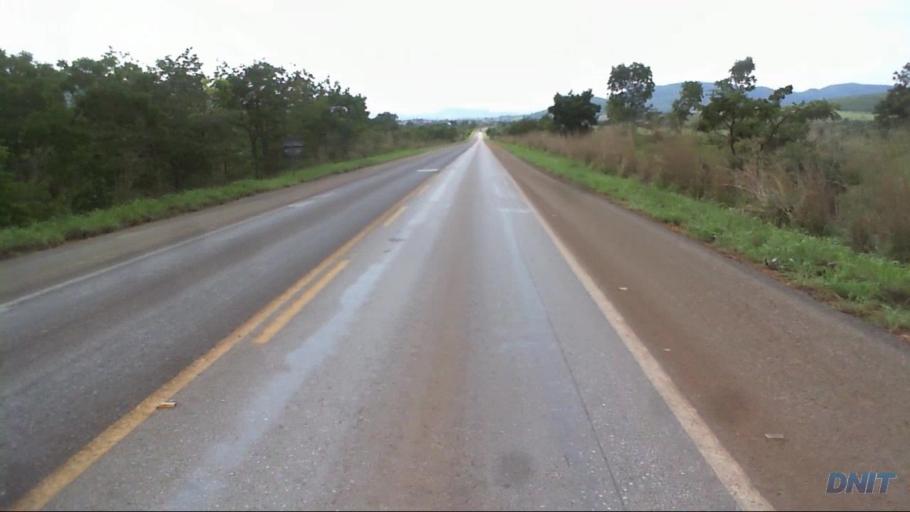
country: BR
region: Goias
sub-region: Barro Alto
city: Barro Alto
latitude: -14.9422
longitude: -48.9379
